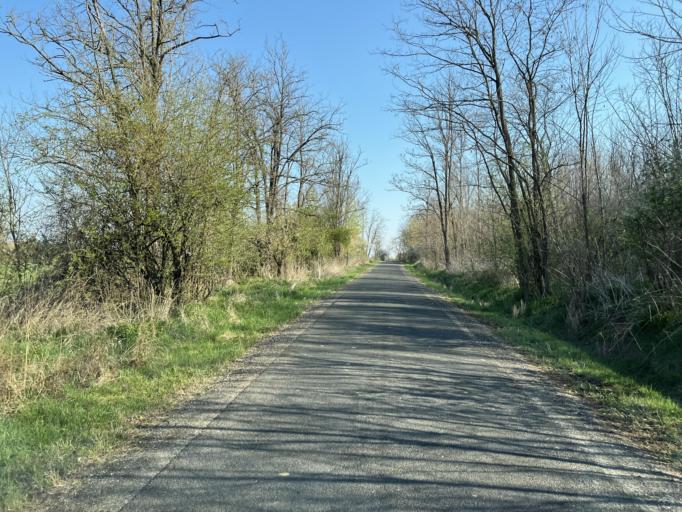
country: SK
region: Nitriansky
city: Sahy
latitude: 48.0139
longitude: 18.8210
